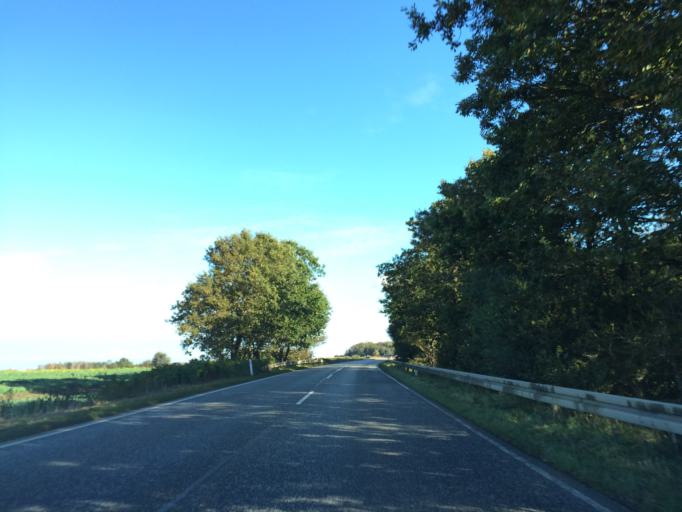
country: DK
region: Central Jutland
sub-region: Randers Kommune
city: Langa
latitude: 56.3738
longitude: 9.9416
